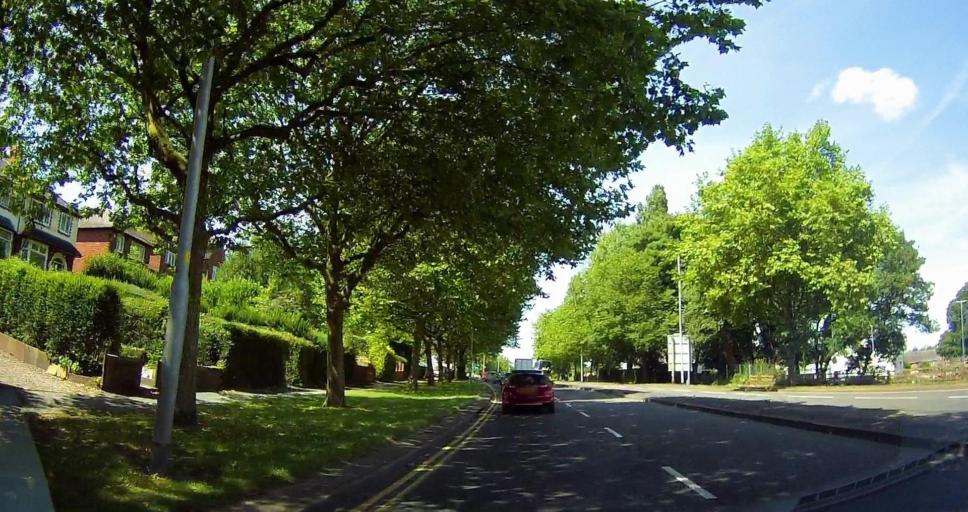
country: GB
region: England
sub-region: Wolverhampton
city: Bilston
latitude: 52.5551
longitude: -2.1013
